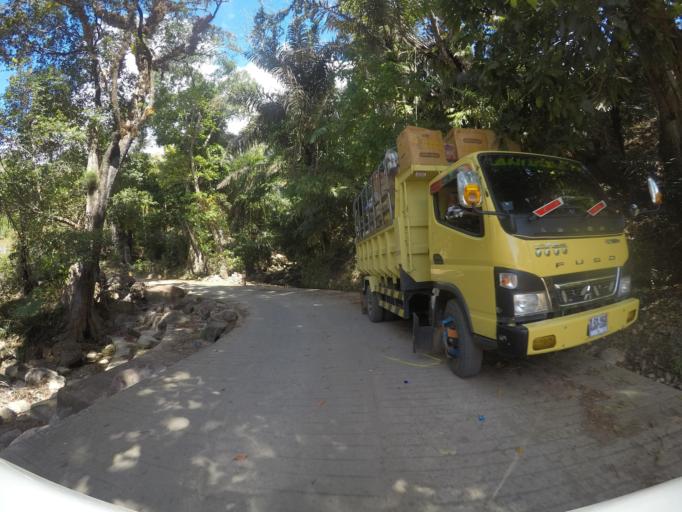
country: TL
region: Lautem
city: Lospalos
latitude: -8.5390
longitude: 126.8013
